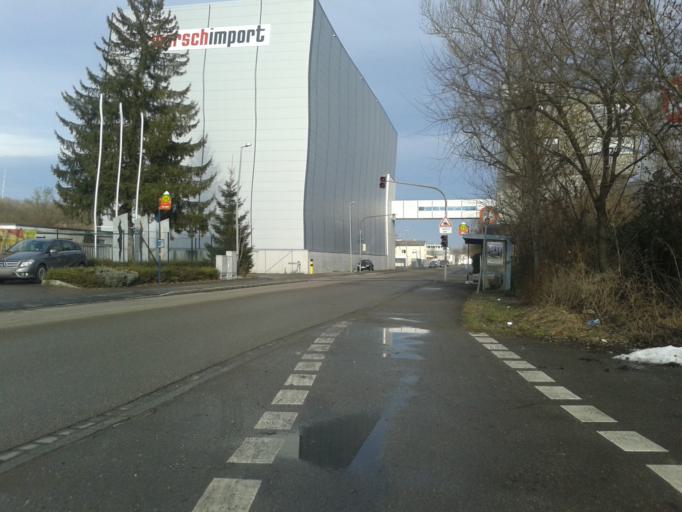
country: DE
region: Baden-Wuerttemberg
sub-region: Tuebingen Region
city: Ulm
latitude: 48.3670
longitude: 9.9437
